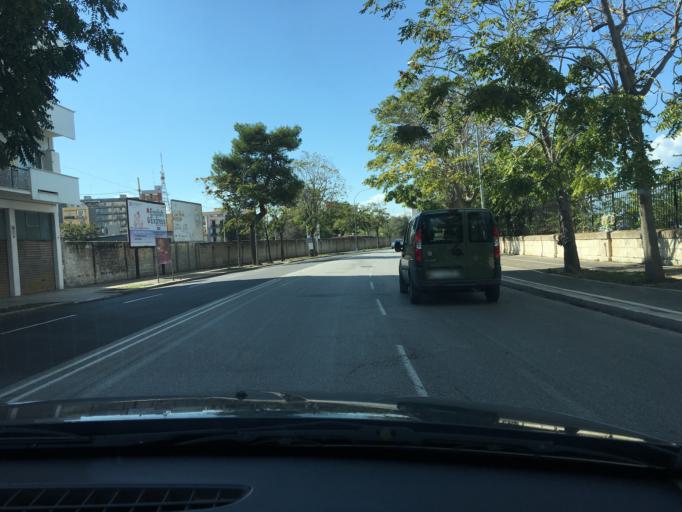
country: IT
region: Apulia
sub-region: Provincia di Bari
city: Bari
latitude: 41.1281
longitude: 16.8546
